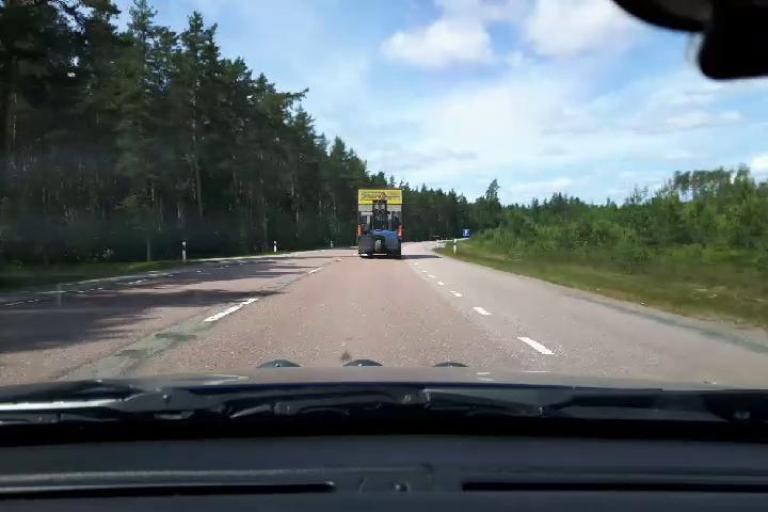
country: SE
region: Uppsala
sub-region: Osthammars Kommun
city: Bjorklinge
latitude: 60.1197
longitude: 17.5126
